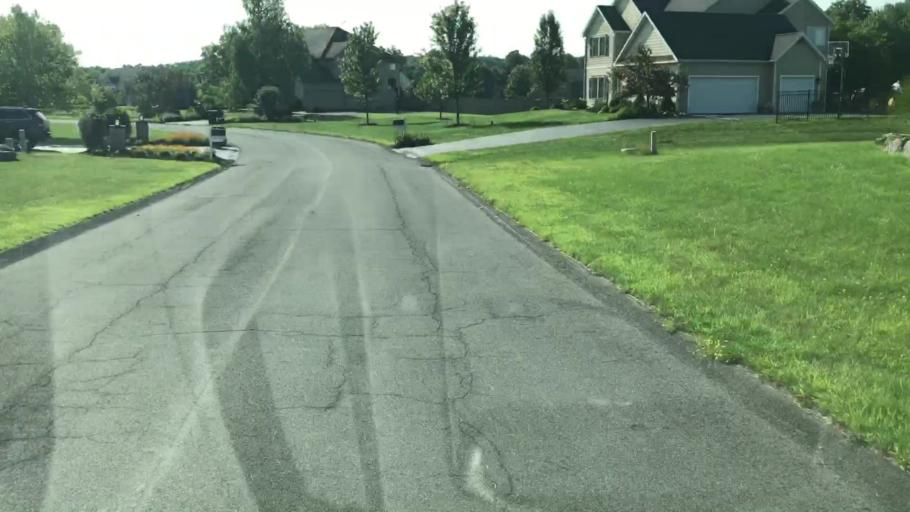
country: US
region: New York
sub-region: Onondaga County
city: Manlius
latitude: 42.9885
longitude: -75.9747
